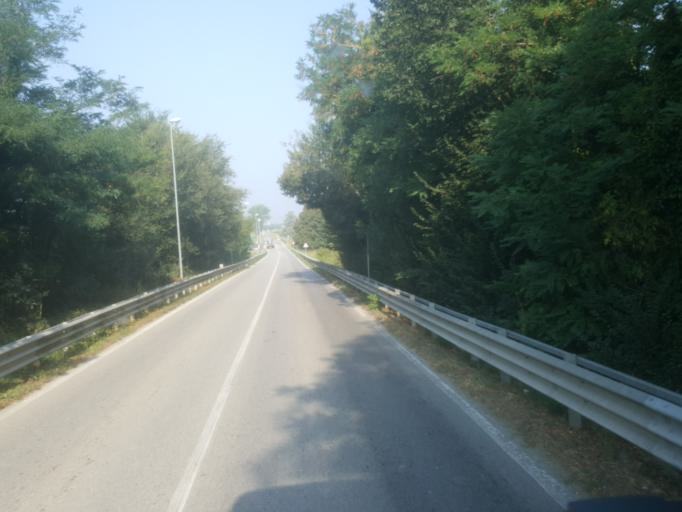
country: IT
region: Emilia-Romagna
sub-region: Provincia di Ravenna
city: Voltana
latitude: 44.5551
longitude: 11.9338
